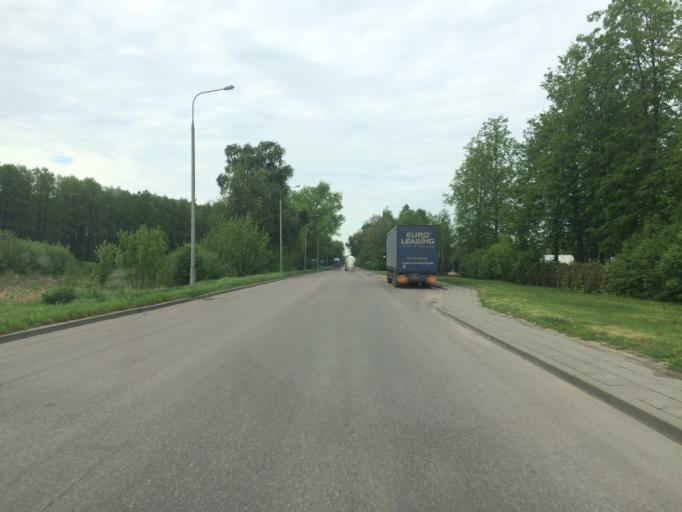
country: PL
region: Masovian Voivodeship
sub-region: Powiat mlawski
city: Mlawa
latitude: 53.1009
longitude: 20.3743
